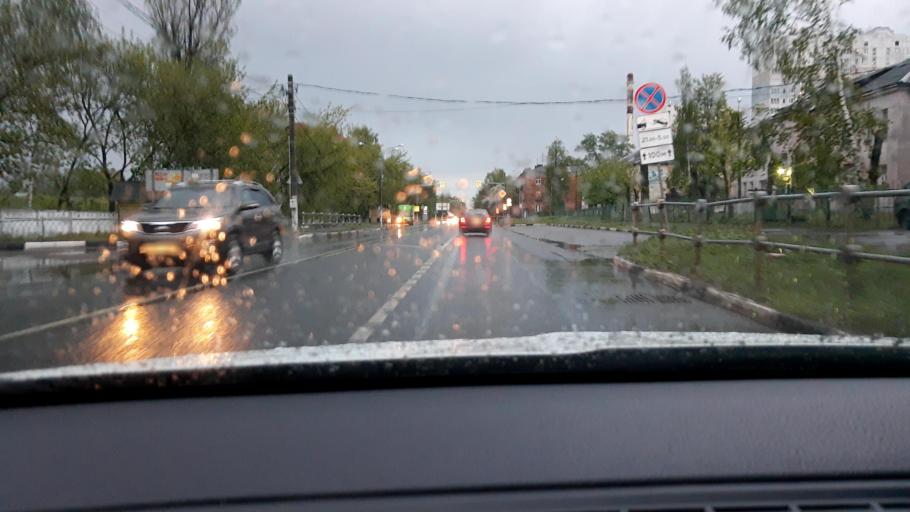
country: RU
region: Moskovskaya
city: Zagoryanskiy
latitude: 55.9268
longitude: 37.9585
